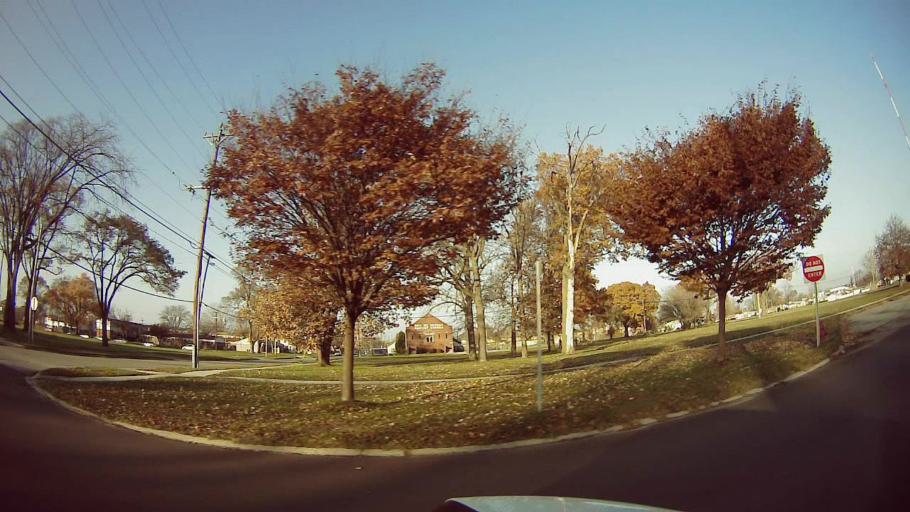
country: US
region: Michigan
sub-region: Oakland County
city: Oak Park
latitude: 42.4483
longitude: -83.1616
